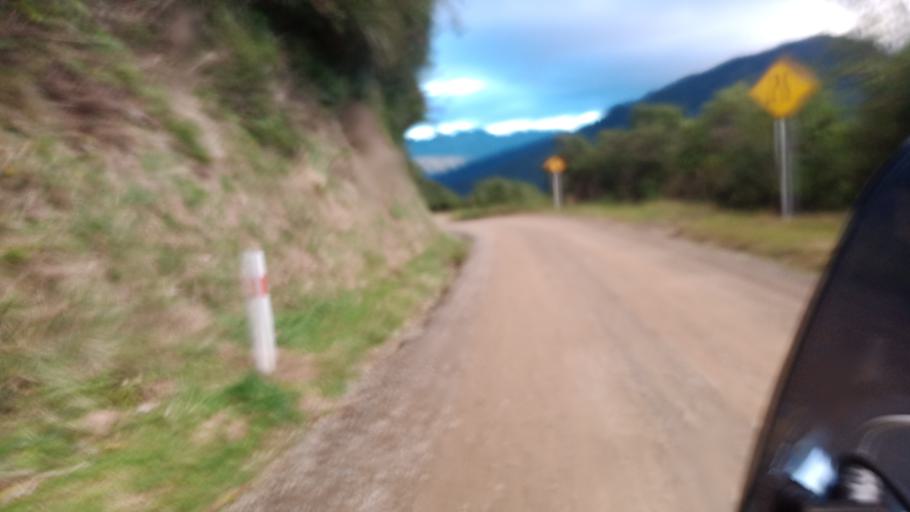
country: NZ
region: Hawke's Bay
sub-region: Wairoa District
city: Wairoa
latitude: -38.7274
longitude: 177.0657
